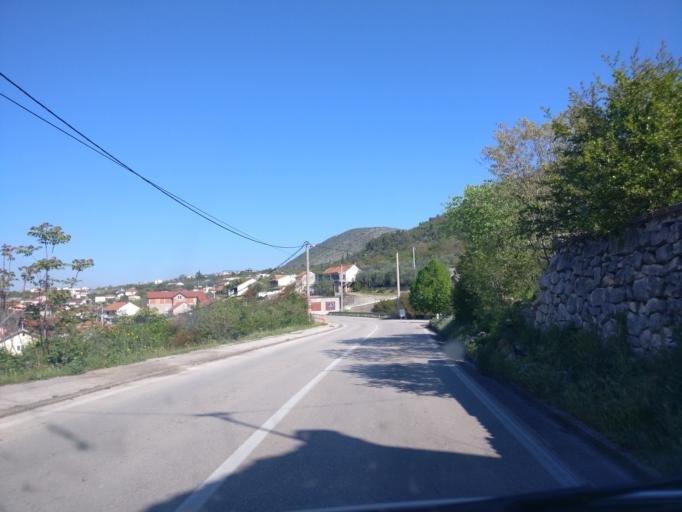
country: BA
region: Federation of Bosnia and Herzegovina
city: Capljina
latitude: 43.1374
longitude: 17.6709
